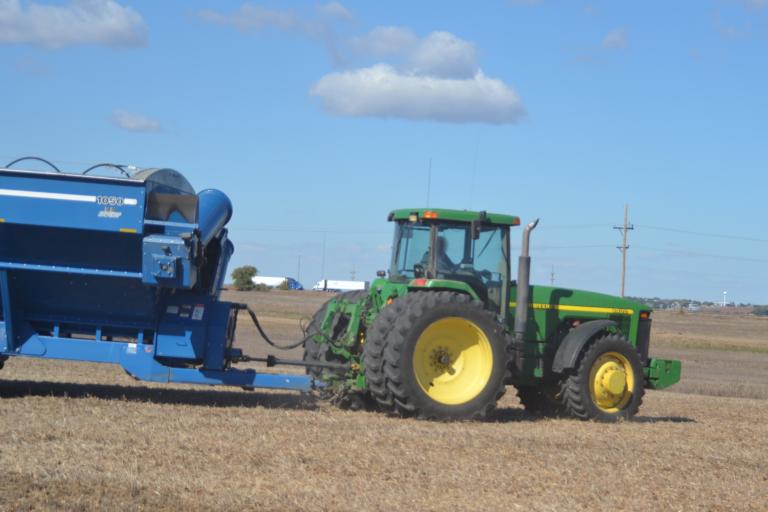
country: US
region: Kansas
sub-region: Barton County
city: Great Bend
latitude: 38.3599
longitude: -98.7016
